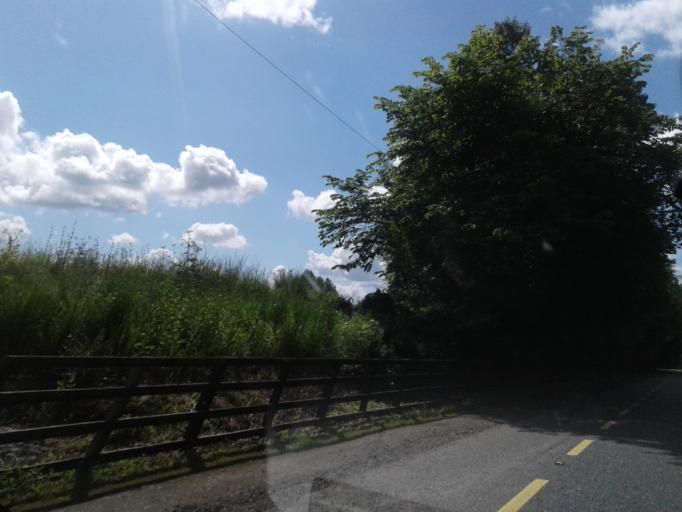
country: IE
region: Leinster
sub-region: An Iarmhi
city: Kilbeggan
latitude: 53.3267
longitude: -7.5118
